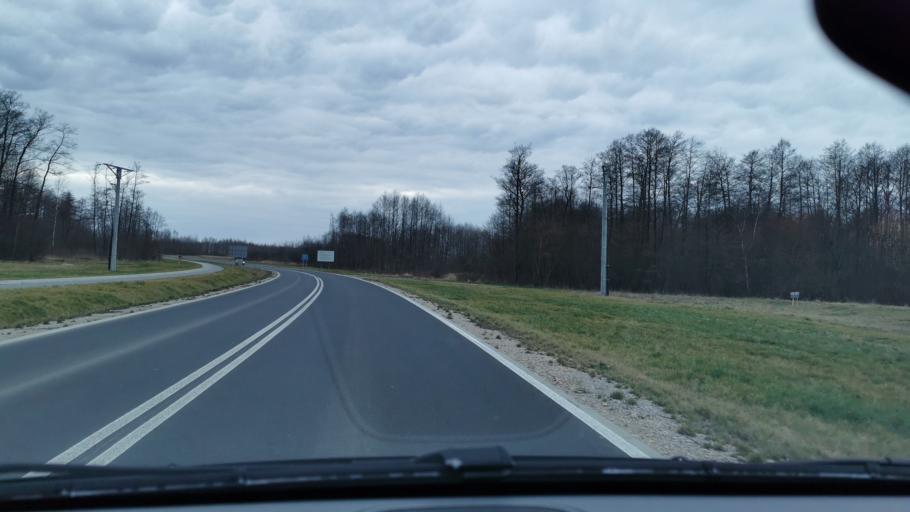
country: PL
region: Masovian Voivodeship
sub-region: Powiat zyrardowski
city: Zyrardow
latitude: 52.0078
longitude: 20.4657
